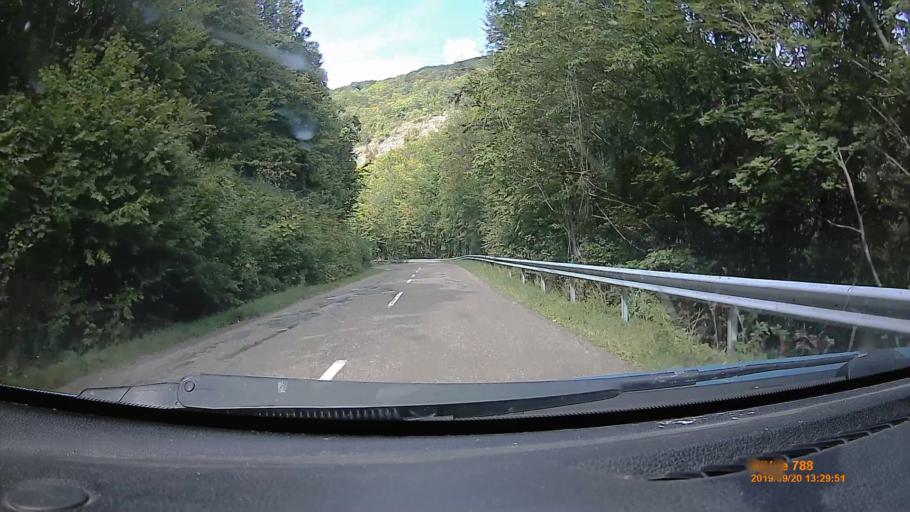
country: HU
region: Heves
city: Szilvasvarad
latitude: 48.0552
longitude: 20.4843
